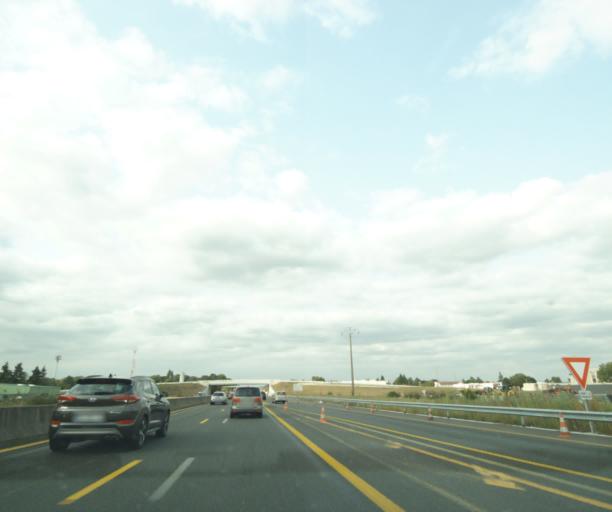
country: FR
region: Centre
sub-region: Departement d'Indre-et-Loire
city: Chambray-les-Tours
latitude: 47.3319
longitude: 0.6943
